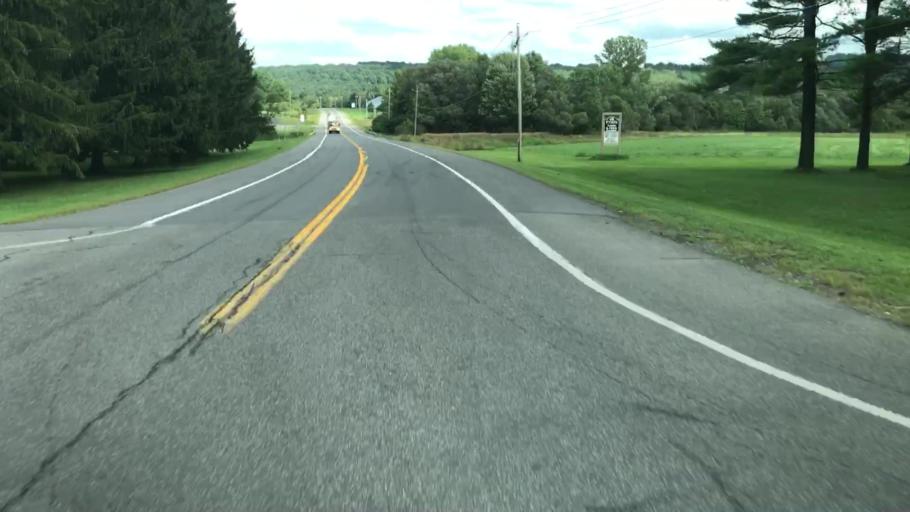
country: US
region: New York
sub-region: Onondaga County
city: Marcellus
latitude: 42.9516
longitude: -76.3520
